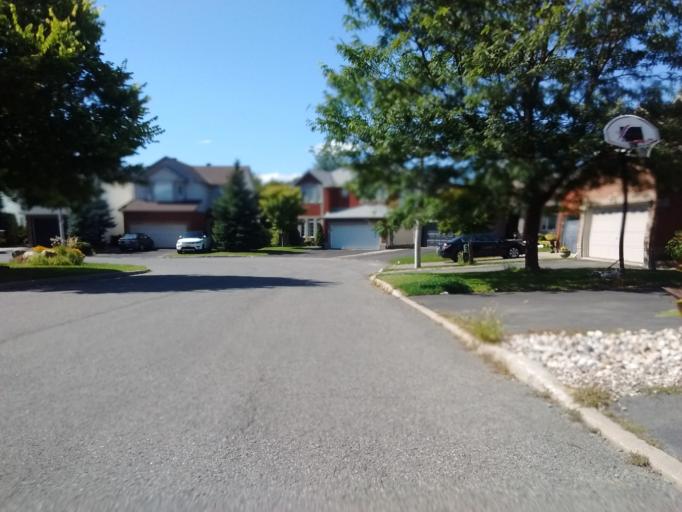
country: CA
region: Ontario
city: Ottawa
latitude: 45.4406
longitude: -75.6353
